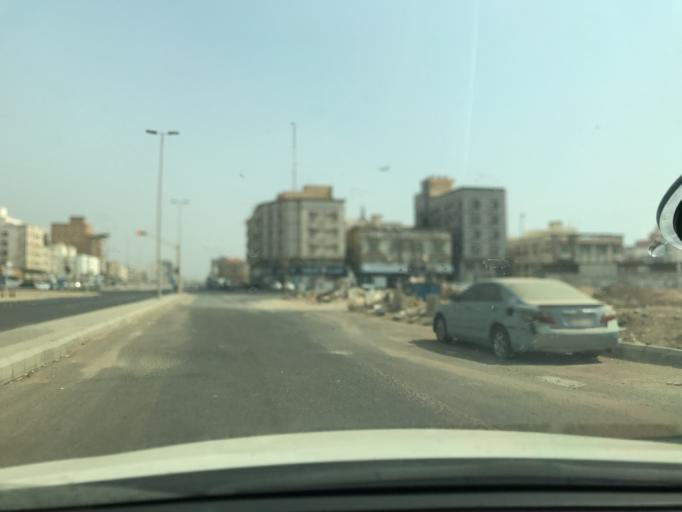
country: SA
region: Makkah
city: Jeddah
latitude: 21.6318
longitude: 39.1605
